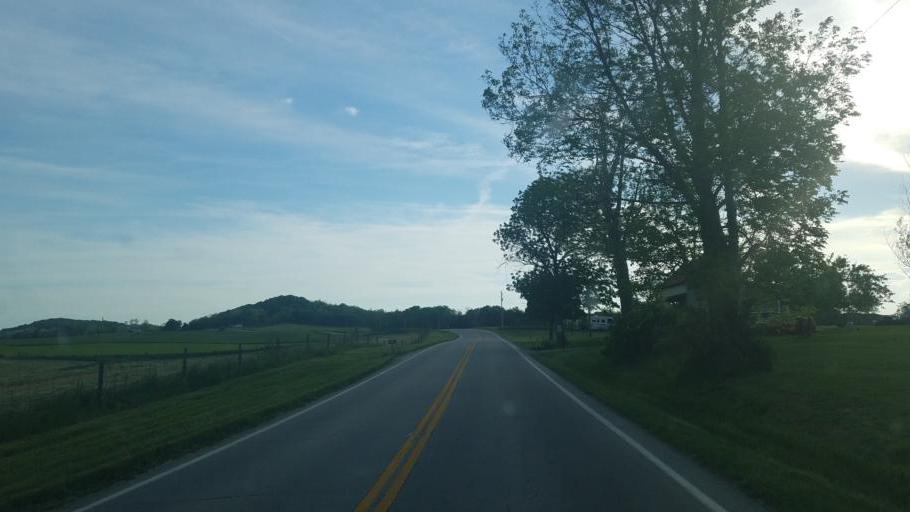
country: US
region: Ohio
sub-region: Ross County
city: Frankfort
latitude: 39.4230
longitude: -83.2626
